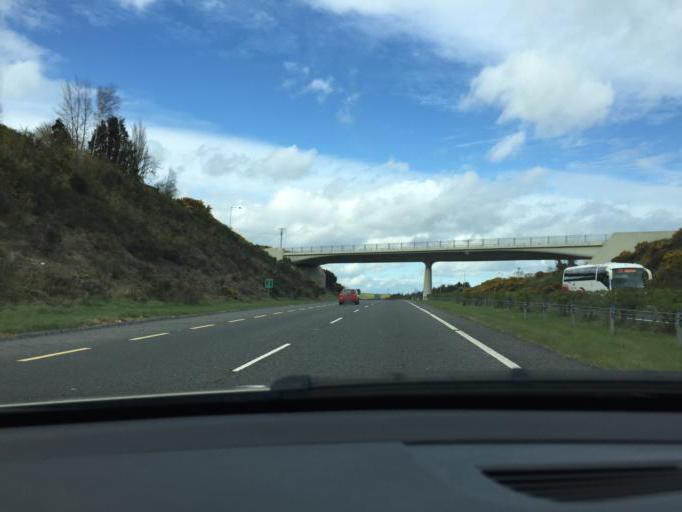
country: IE
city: Newtownmountkennedy
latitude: 53.0639
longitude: -6.0925
